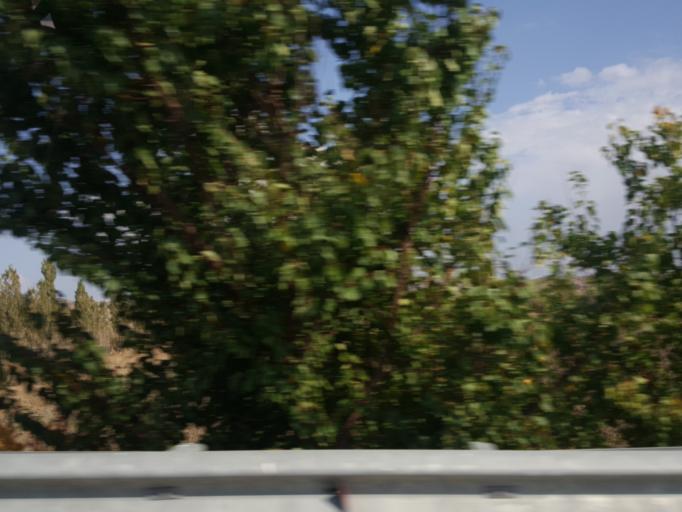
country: TR
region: Corum
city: Sungurlu
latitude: 40.1762
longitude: 34.4658
